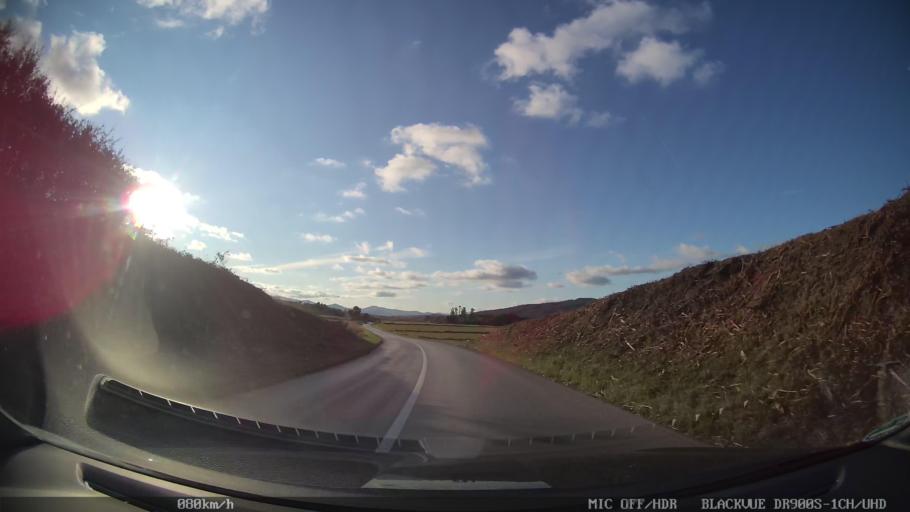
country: HR
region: Karlovacka
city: Plaski
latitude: 45.0916
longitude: 15.3594
